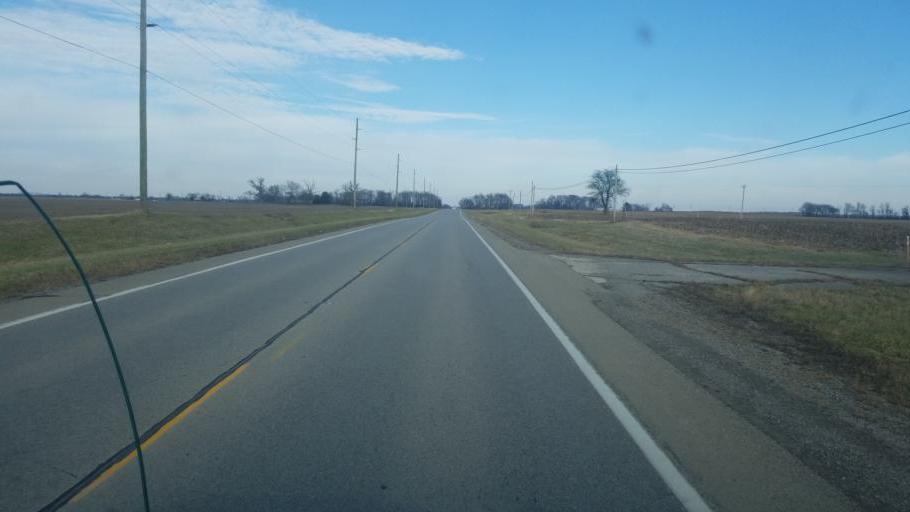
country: US
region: Illinois
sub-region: White County
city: Carmi
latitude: 38.1138
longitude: -88.1179
